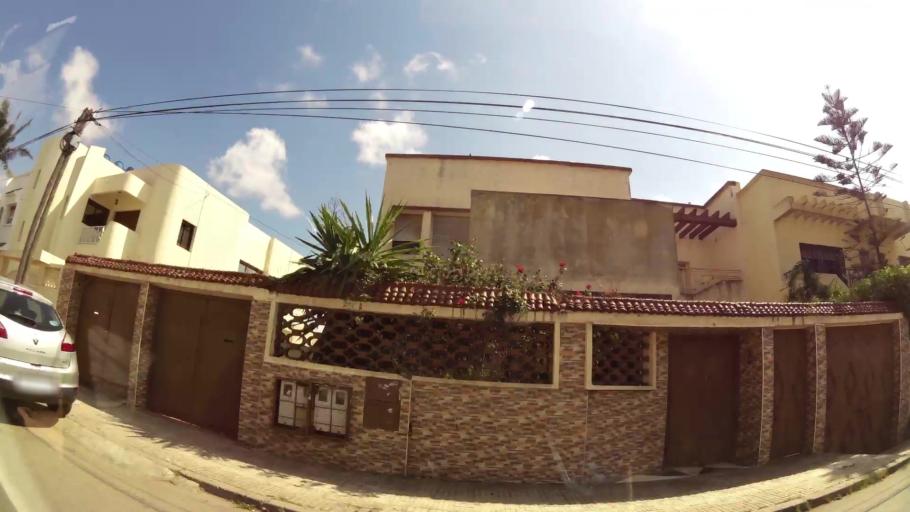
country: MA
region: Rabat-Sale-Zemmour-Zaer
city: Sale
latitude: 34.0390
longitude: -6.7917
